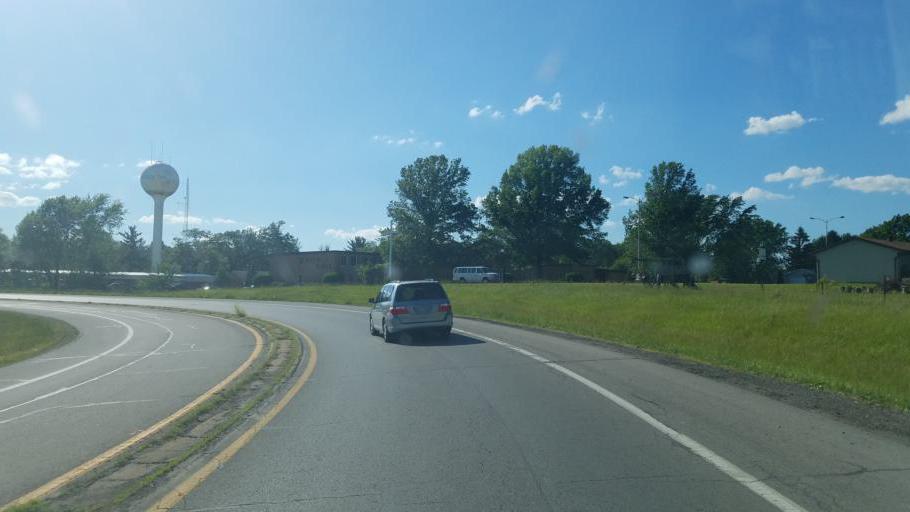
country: US
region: Ohio
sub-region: Richland County
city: Lincoln Heights
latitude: 40.7809
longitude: -82.4707
